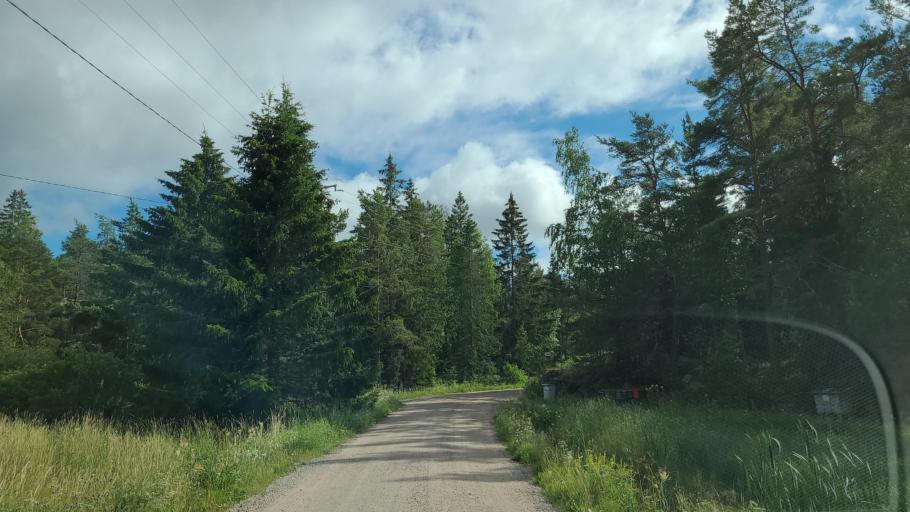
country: FI
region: Varsinais-Suomi
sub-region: Aboland-Turunmaa
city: Nagu
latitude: 60.1974
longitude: 21.7759
